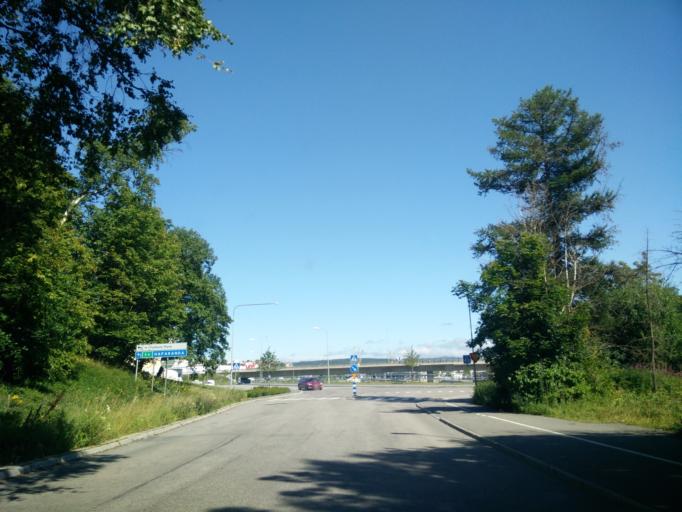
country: SE
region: Vaesternorrland
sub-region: Haernoesands Kommun
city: Haernoesand
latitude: 62.6324
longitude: 17.9233
